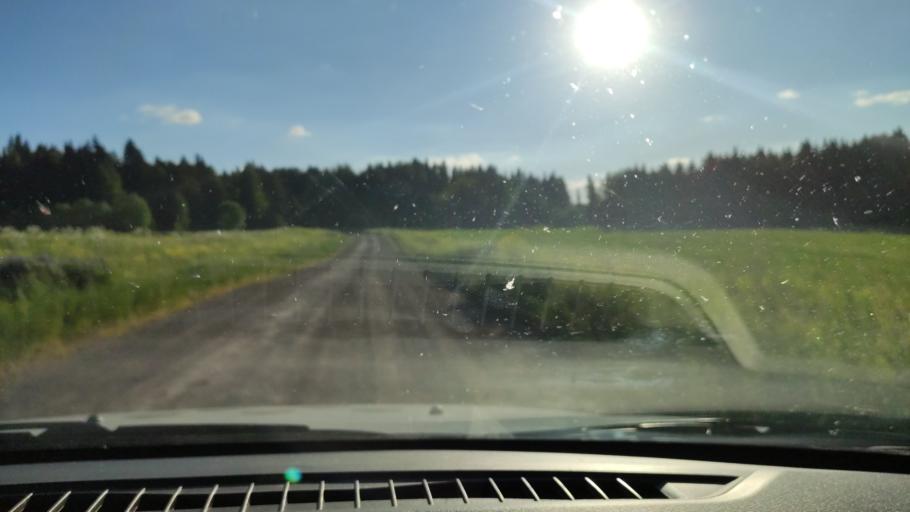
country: RU
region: Perm
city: Orda
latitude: 57.3005
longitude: 56.5908
